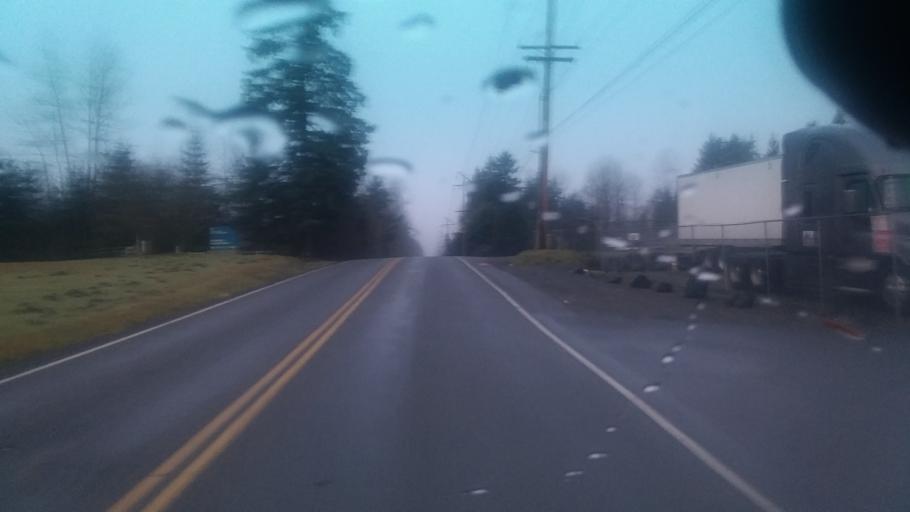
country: US
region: Washington
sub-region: Pierce County
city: South Hill
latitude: 47.1257
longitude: -122.2953
